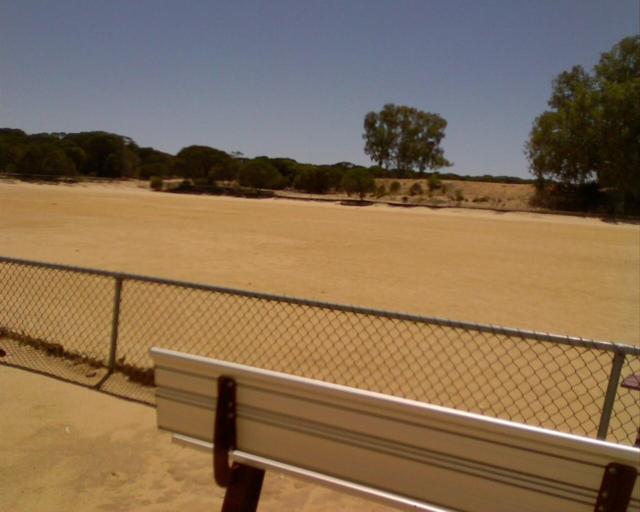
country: AU
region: Western Australia
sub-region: Wongan-Ballidu
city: Wongan Hills
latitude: -30.8195
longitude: 117.4842
